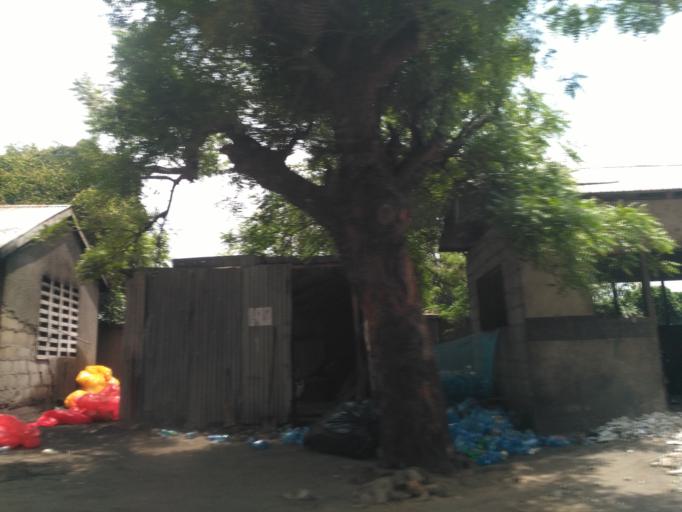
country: TZ
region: Dar es Salaam
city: Dar es Salaam
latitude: -6.8045
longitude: 39.2711
